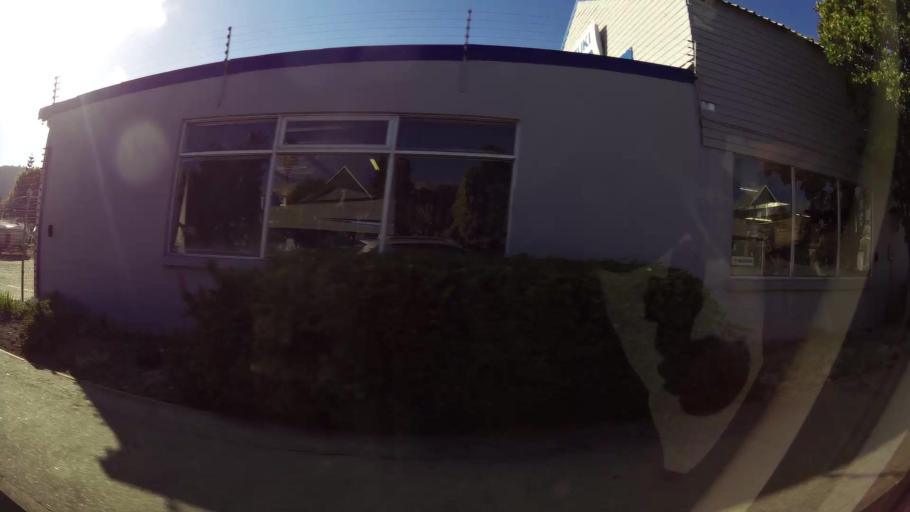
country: ZA
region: Western Cape
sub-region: Eden District Municipality
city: Knysna
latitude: -34.0412
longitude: 23.0485
